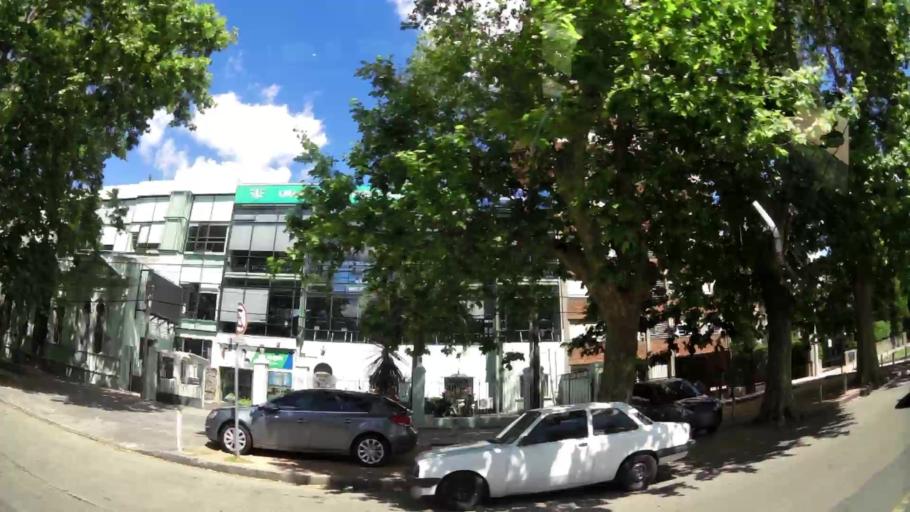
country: UY
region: Montevideo
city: Montevideo
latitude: -34.8730
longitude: -56.1965
